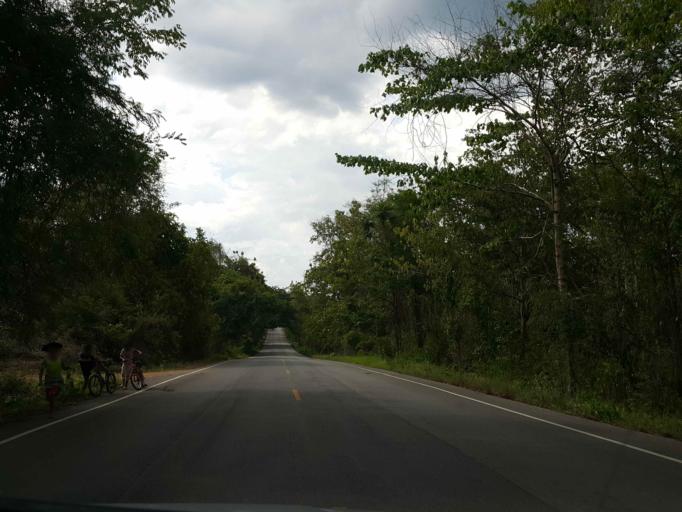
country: TH
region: Sukhothai
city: Thung Saliam
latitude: 17.3827
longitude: 99.3996
